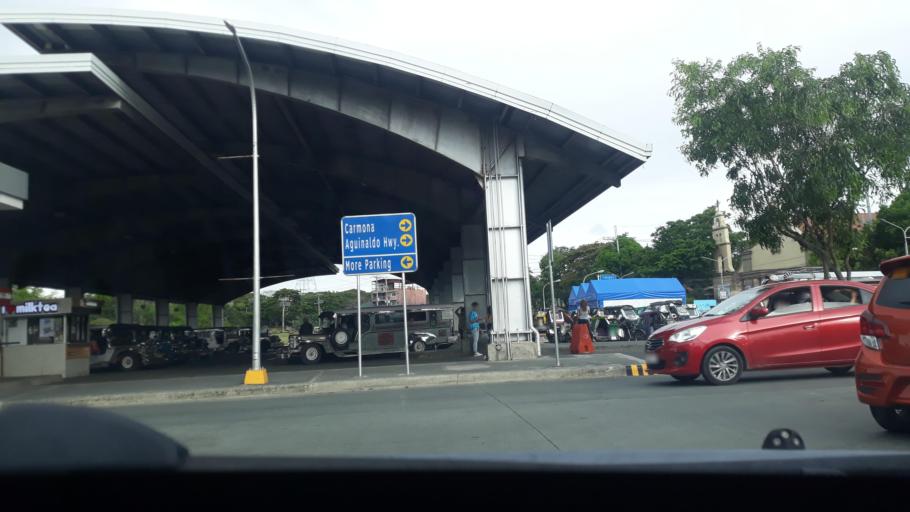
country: PH
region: Calabarzon
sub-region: Province of Cavite
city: Dasmarinas
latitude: 14.3002
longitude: 120.9575
